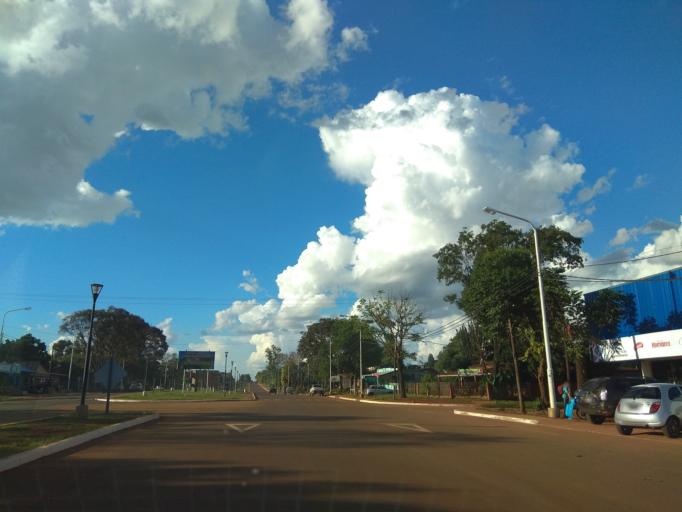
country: AR
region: Misiones
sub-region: Departamento de Candelaria
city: Candelaria
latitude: -27.4698
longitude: -55.7457
